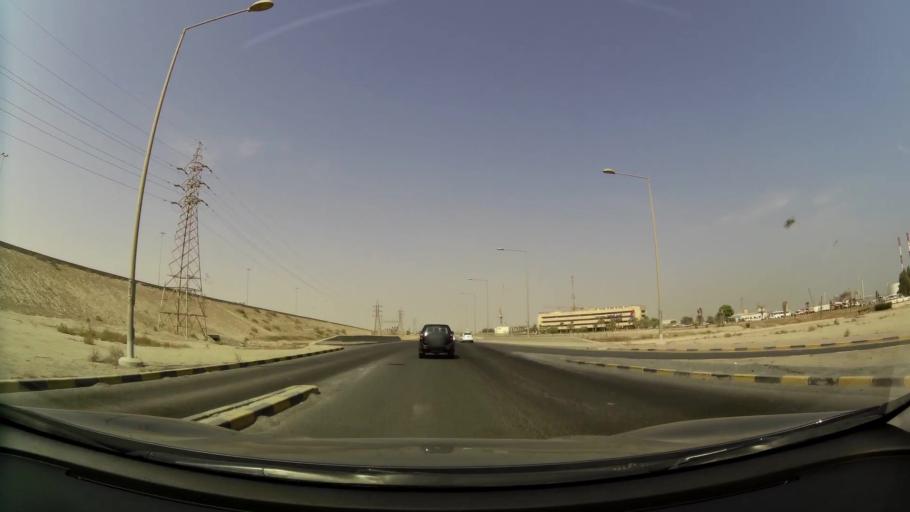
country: KW
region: Al Ahmadi
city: Al Fahahil
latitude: 28.9970
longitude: 48.1435
